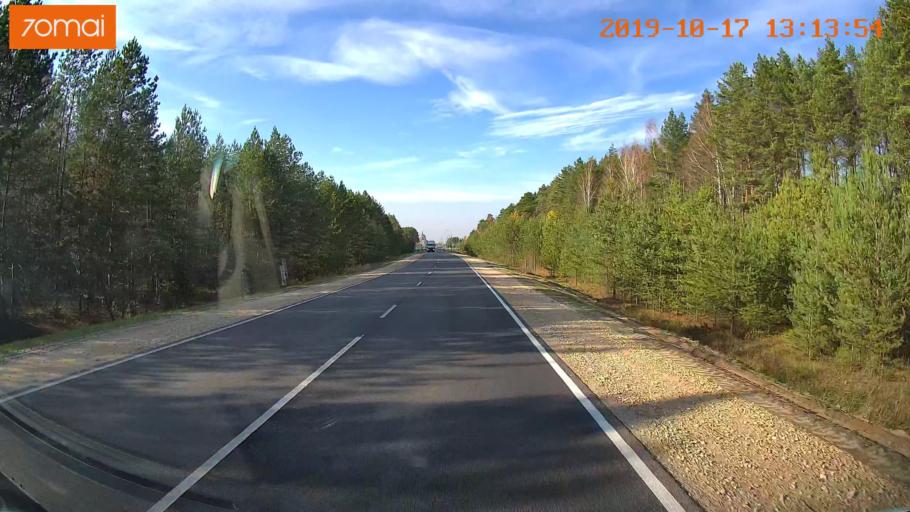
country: RU
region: Rjazan
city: Gus'-Zheleznyy
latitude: 55.0487
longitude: 41.1818
